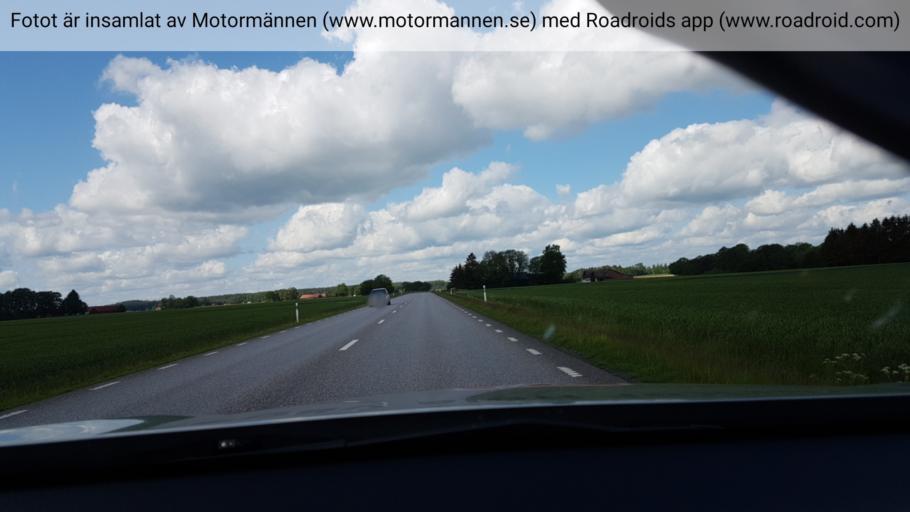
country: SE
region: Vaestra Goetaland
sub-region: Vara Kommun
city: Vara
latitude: 58.3001
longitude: 12.9048
